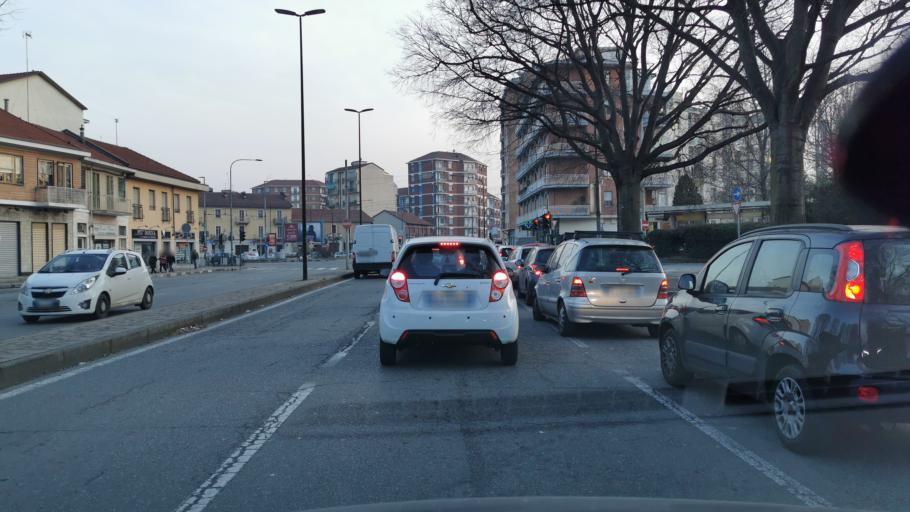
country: IT
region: Piedmont
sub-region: Provincia di Torino
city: Venaria Reale
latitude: 45.0999
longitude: 7.6485
